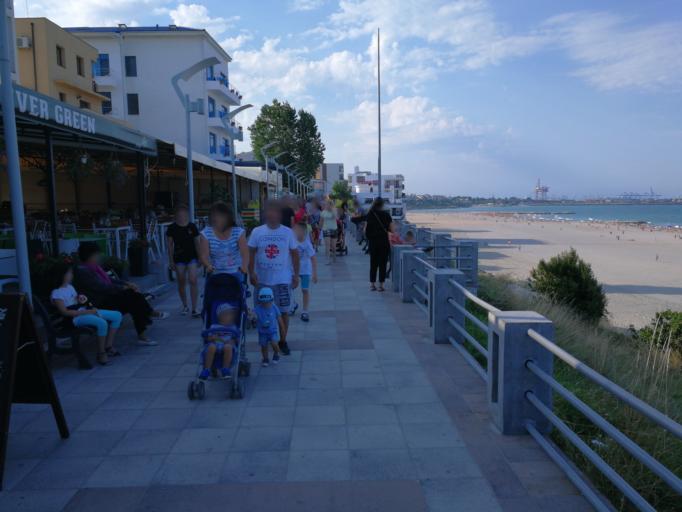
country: RO
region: Constanta
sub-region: Oras Eforie
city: Eforie Nord
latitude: 44.0689
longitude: 28.6386
